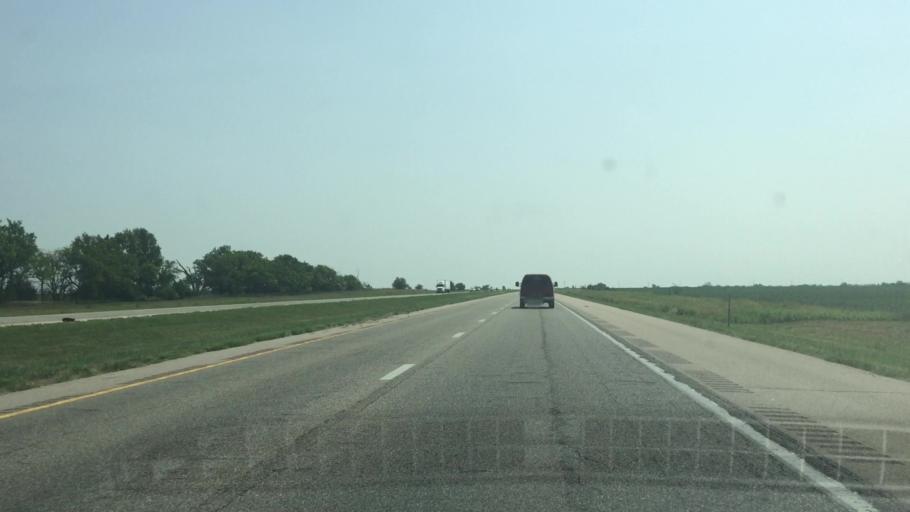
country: US
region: Kansas
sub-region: Osage County
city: Osage City
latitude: 38.4286
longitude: -95.8187
